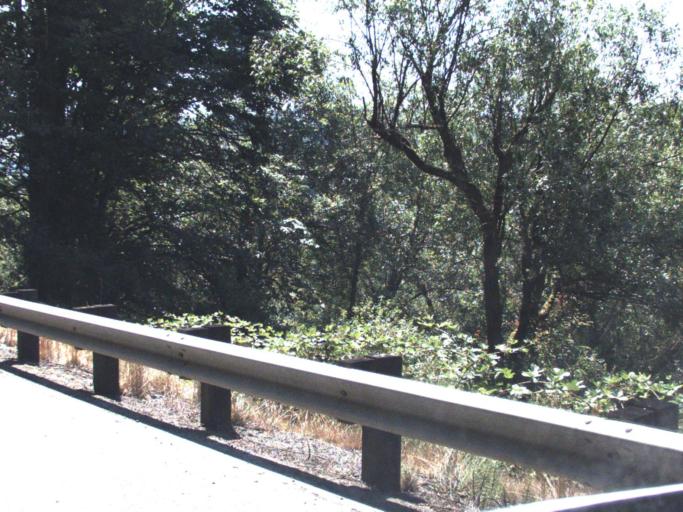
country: US
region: Washington
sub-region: King County
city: Ames Lake
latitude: 47.5871
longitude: -121.9510
